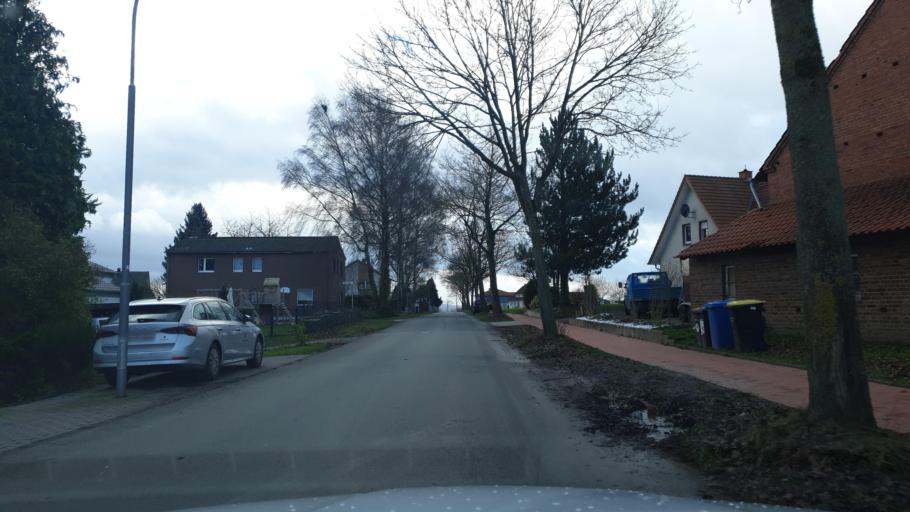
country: DE
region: North Rhine-Westphalia
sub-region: Regierungsbezirk Detmold
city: Hille
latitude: 52.2657
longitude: 8.7507
